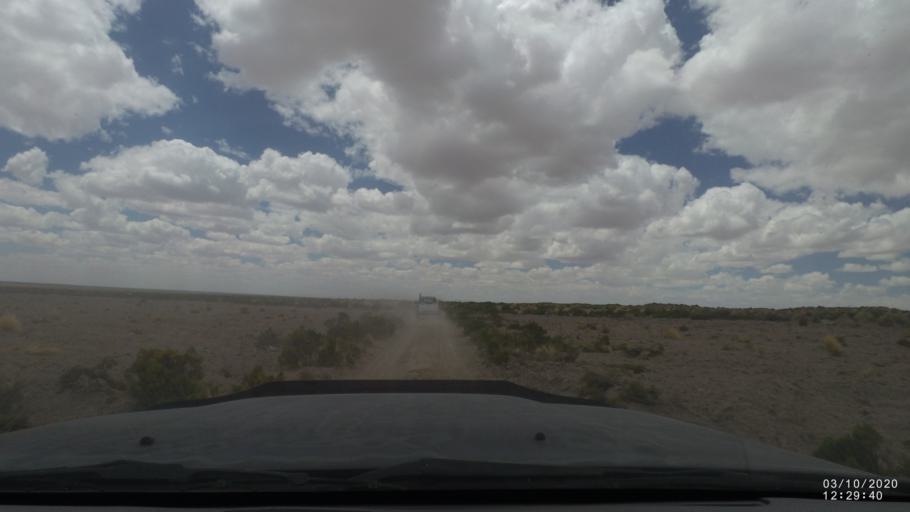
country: BO
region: Oruro
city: Poopo
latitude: -18.6887
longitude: -67.5469
